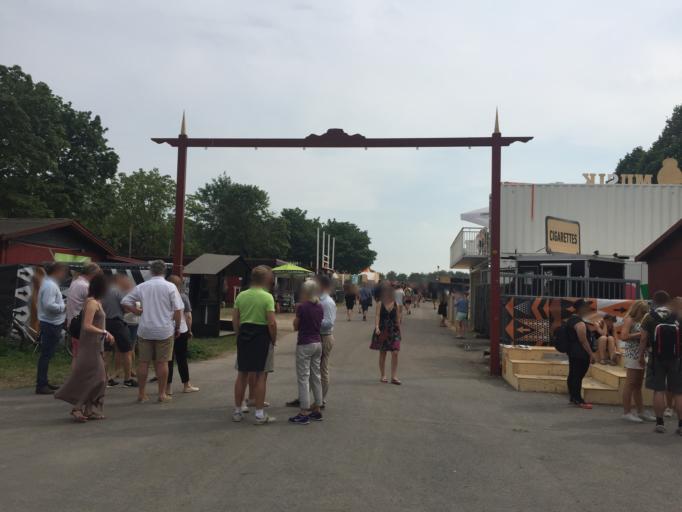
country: DK
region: Zealand
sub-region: Roskilde Kommune
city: Roskilde
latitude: 55.6221
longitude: 12.0790
